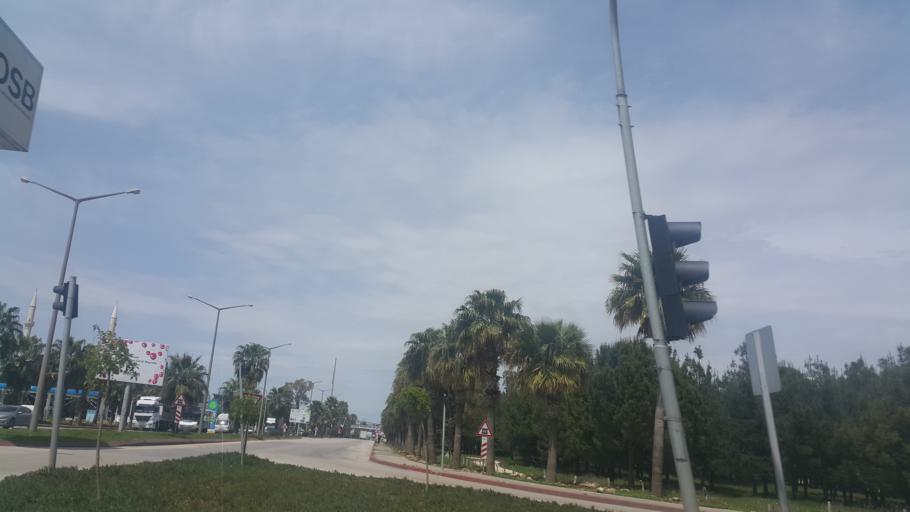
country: TR
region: Adana
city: Yakapinar
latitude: 36.9665
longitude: 35.5920
